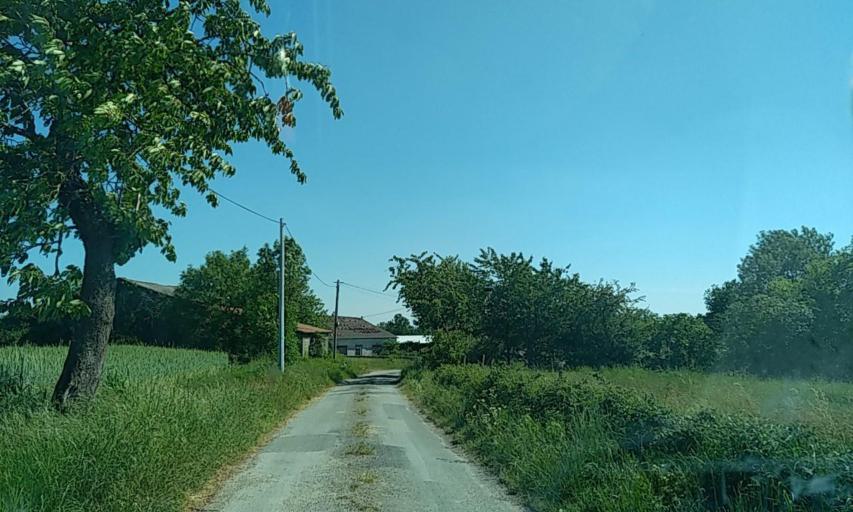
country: FR
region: Poitou-Charentes
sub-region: Departement des Deux-Sevres
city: La Chapelle-Saint-Laurent
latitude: 46.7694
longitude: -0.4820
